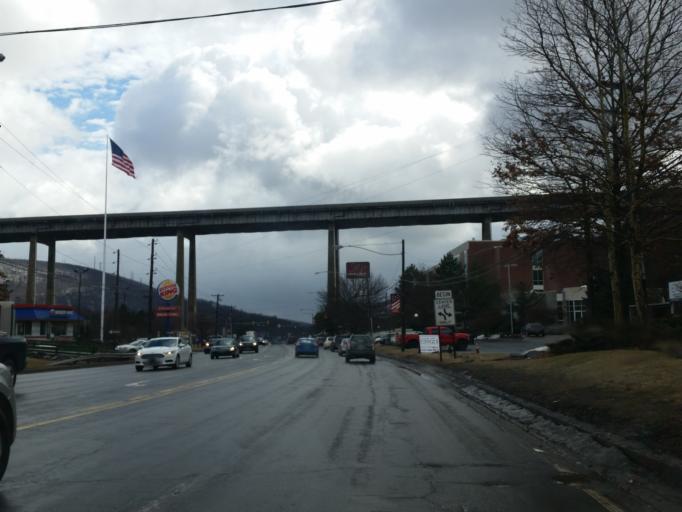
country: US
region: Pennsylvania
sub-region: Lackawanna County
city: Clarks Green
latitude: 41.4851
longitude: -75.6937
